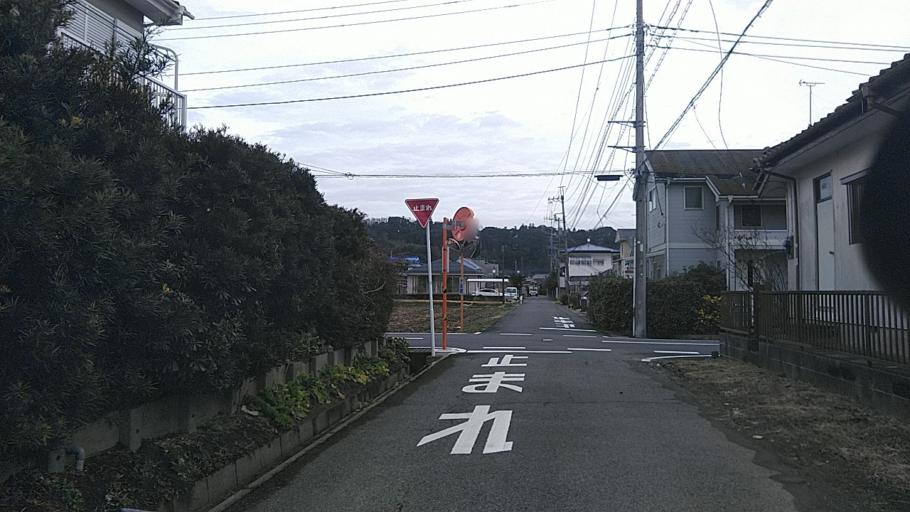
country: JP
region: Chiba
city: Togane
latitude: 35.5572
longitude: 140.3448
